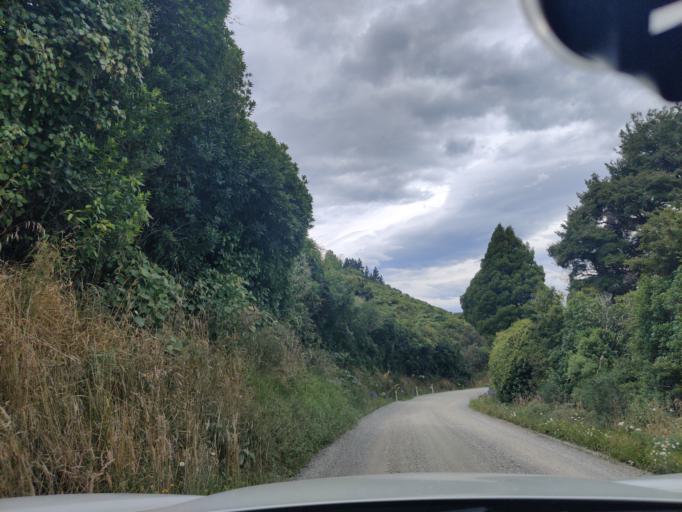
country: NZ
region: Wellington
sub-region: Masterton District
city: Masterton
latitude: -41.0396
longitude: 175.4116
